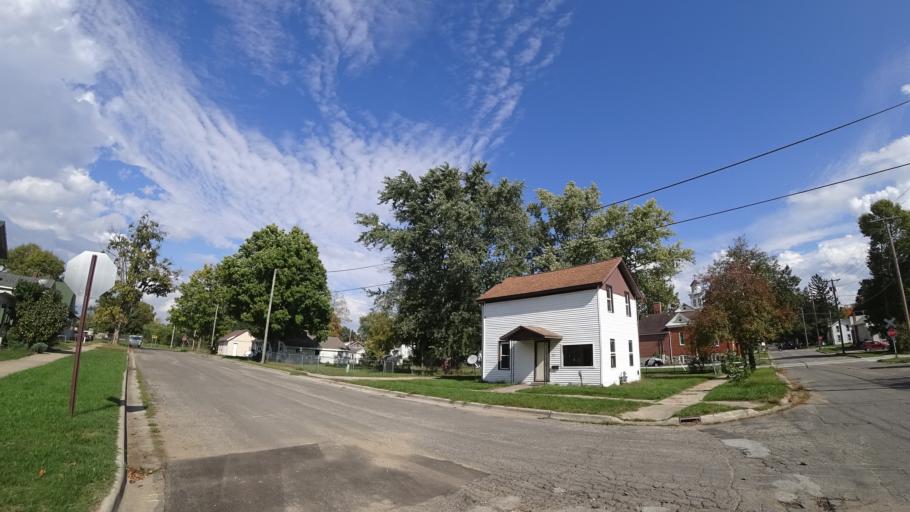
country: US
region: Michigan
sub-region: Saint Joseph County
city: Three Rivers
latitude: 41.9342
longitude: -85.6284
